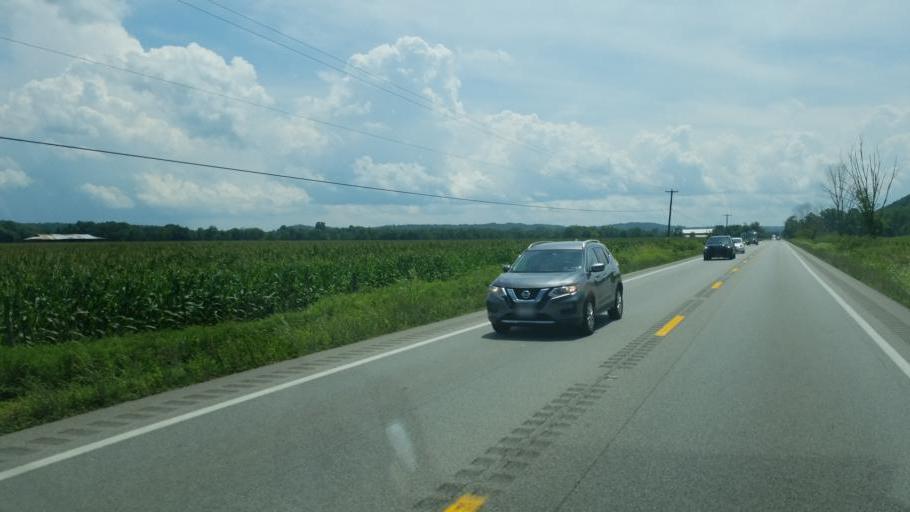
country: US
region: West Virginia
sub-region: Putnam County
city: Buffalo
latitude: 38.6633
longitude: -81.9682
